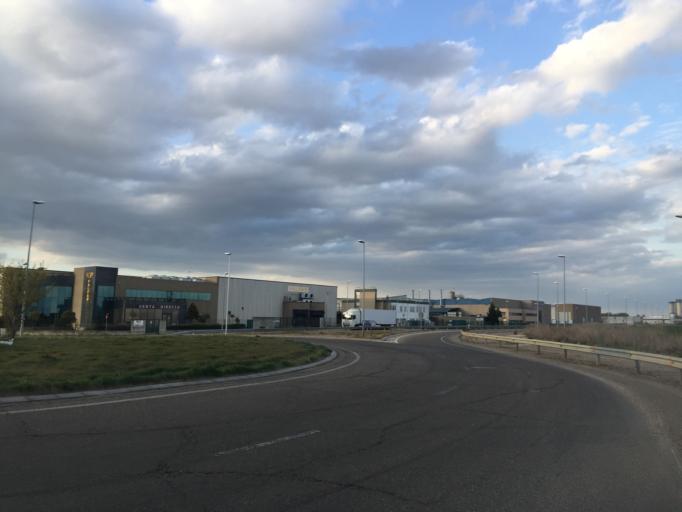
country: ES
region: Castille and Leon
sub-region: Provincia de Palencia
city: Venta de Banos
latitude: 41.9301
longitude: -4.4836
